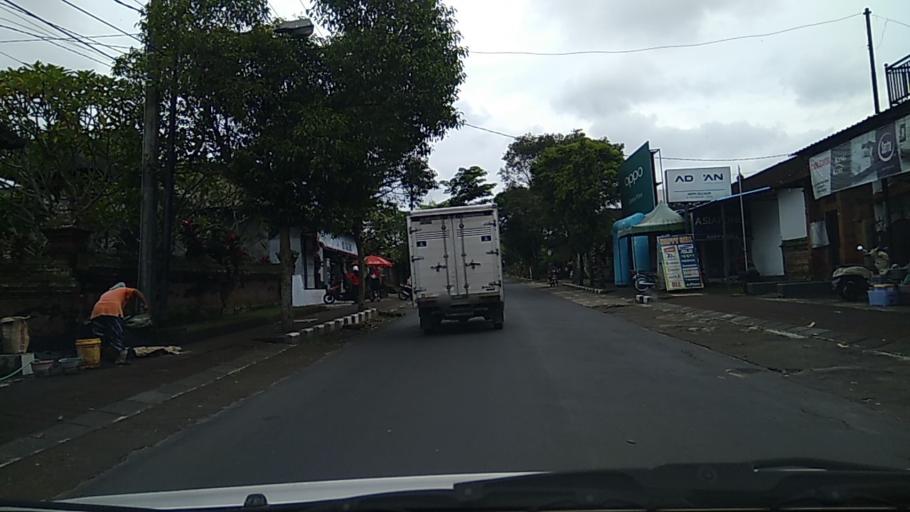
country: ID
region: Bali
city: Brahmana
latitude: -8.4896
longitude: 115.2100
